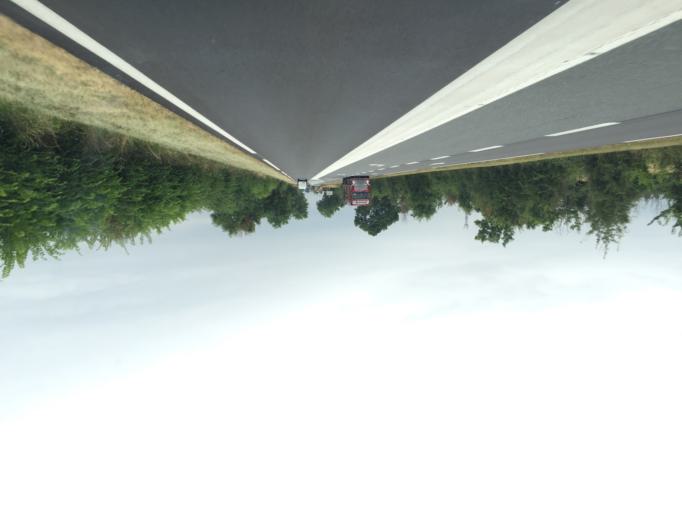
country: FR
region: Auvergne
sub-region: Departement de l'Allier
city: Brout-Vernet
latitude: 46.1958
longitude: 3.2684
